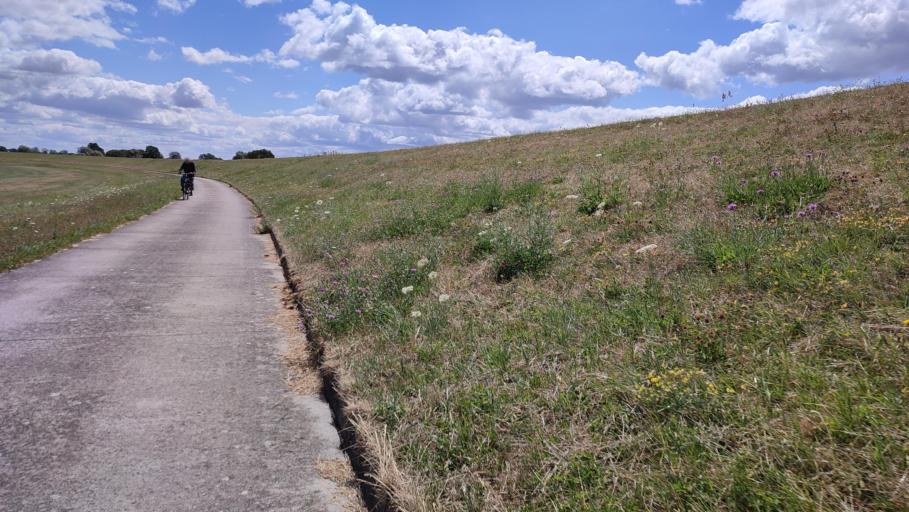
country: DE
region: Lower Saxony
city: Hitzacker
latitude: 53.1932
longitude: 10.9872
